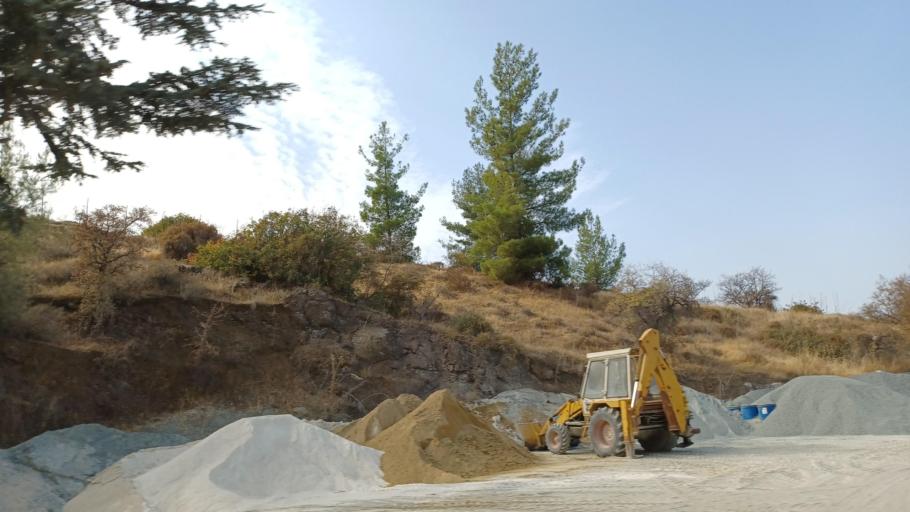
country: CY
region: Lefkosia
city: Kakopetria
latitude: 35.0272
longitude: 32.9008
